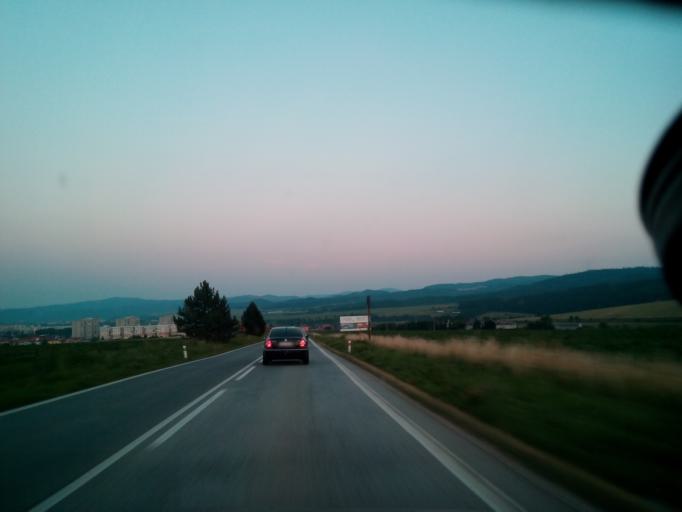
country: SK
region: Kosicky
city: Spisska Nova Ves
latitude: 48.9635
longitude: 20.5031
